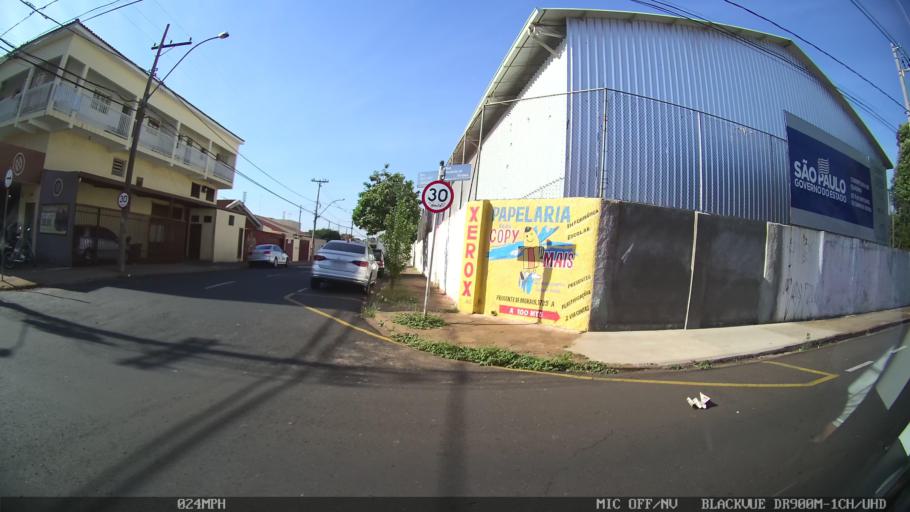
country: BR
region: Sao Paulo
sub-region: Sao Jose Do Rio Preto
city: Sao Jose do Rio Preto
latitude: -20.8008
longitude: -49.3878
